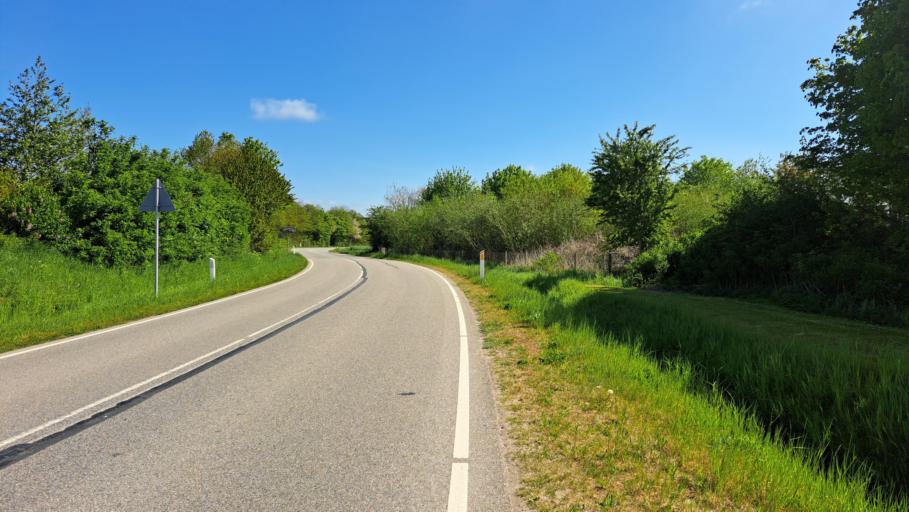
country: DK
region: Central Jutland
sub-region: Hedensted Kommune
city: Hedensted
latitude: 55.7987
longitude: 9.6525
